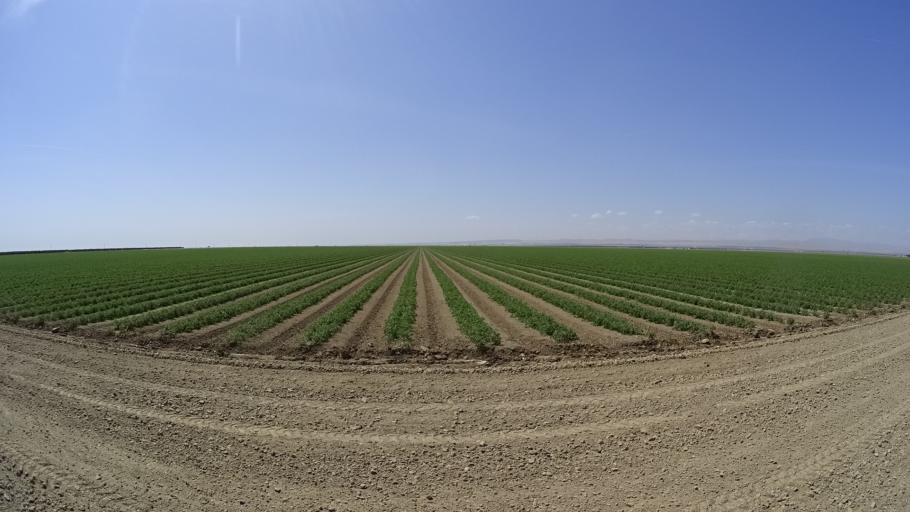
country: US
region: California
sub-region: Kings County
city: Kettleman City
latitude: 36.1377
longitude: -119.9734
